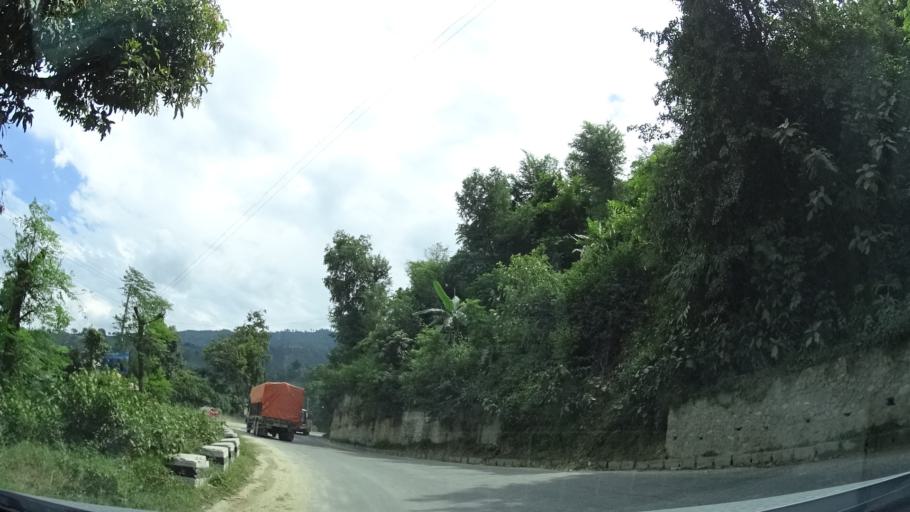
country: NP
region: Central Region
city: Kirtipur
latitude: 27.8031
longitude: 84.9704
